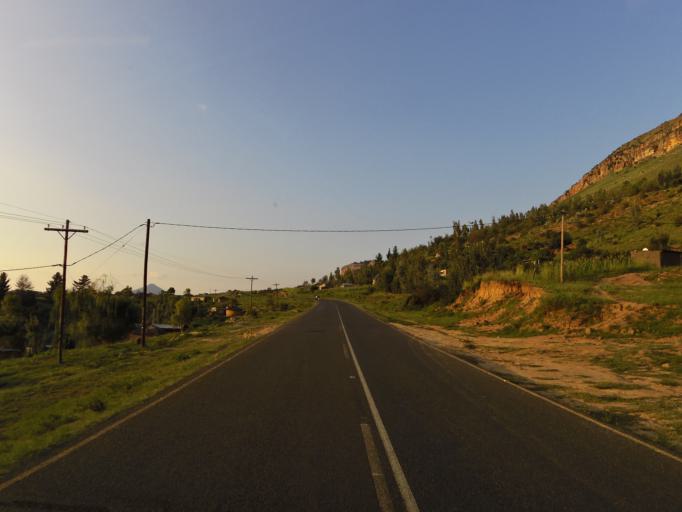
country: LS
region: Leribe
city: Leribe
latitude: -28.9674
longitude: 28.1727
